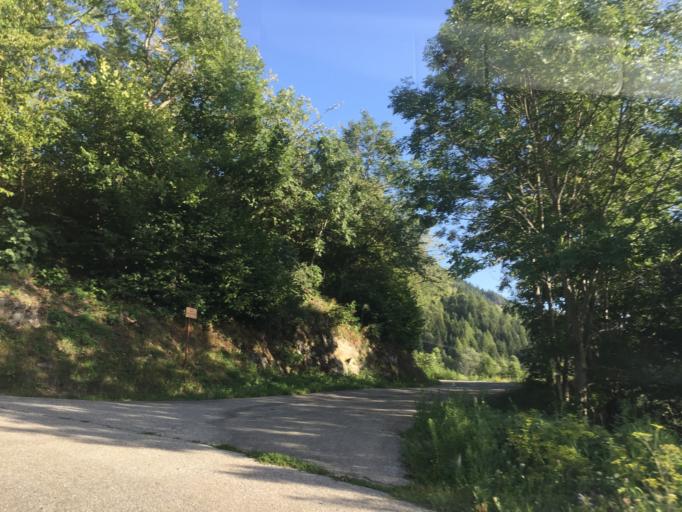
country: FR
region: Rhone-Alpes
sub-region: Departement de la Savoie
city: Moutiers
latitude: 45.5102
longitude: 6.5913
